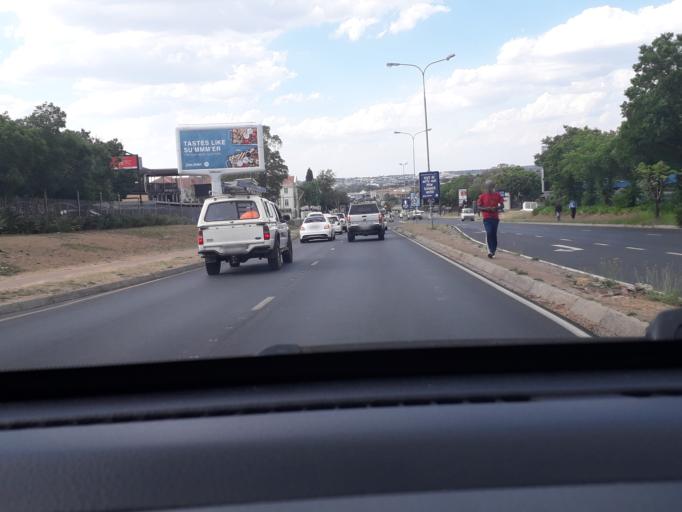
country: ZA
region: Gauteng
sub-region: City of Johannesburg Metropolitan Municipality
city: Midrand
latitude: -26.0451
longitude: 28.0596
